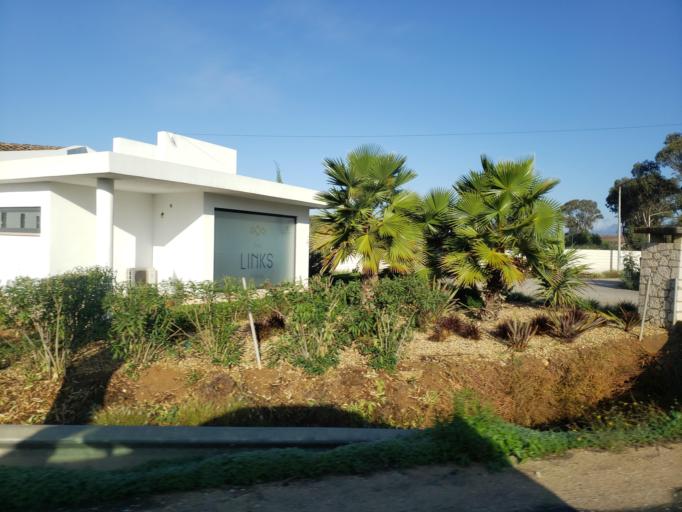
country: PT
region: Faro
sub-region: Portimao
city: Alvor
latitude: 37.1593
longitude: -8.5709
